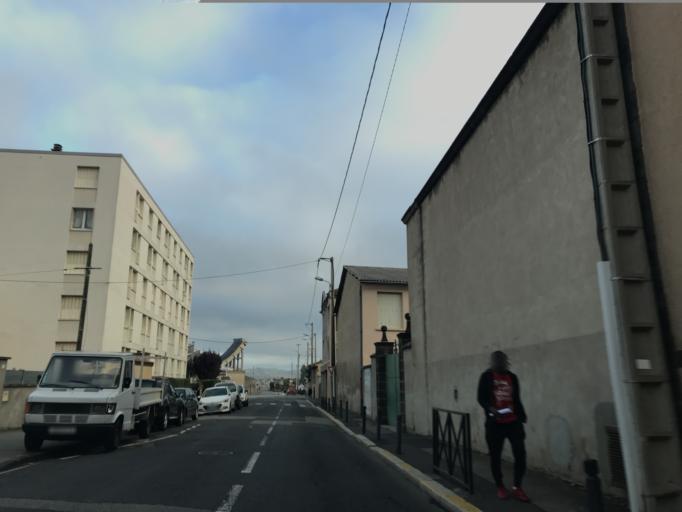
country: FR
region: Auvergne
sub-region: Departement du Puy-de-Dome
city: Clermont-Ferrand
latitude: 45.7957
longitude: 3.1129
